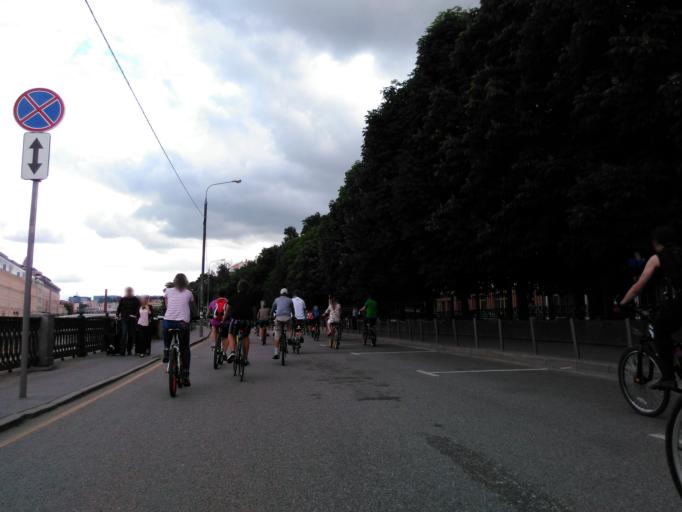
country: RU
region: Moscow
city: Zamoskvorech'ye
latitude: 55.7385
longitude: 37.6386
